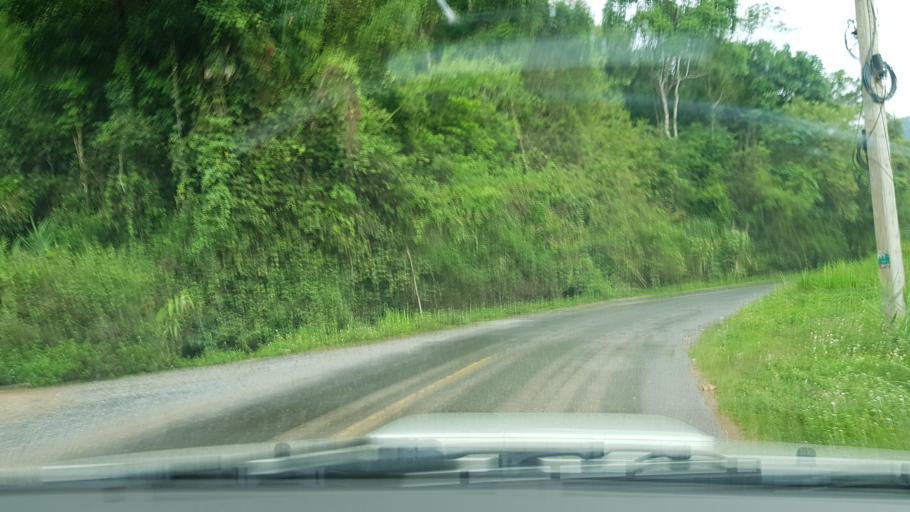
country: LA
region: Oudomxai
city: Muang Xay
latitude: 20.5946
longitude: 101.9365
